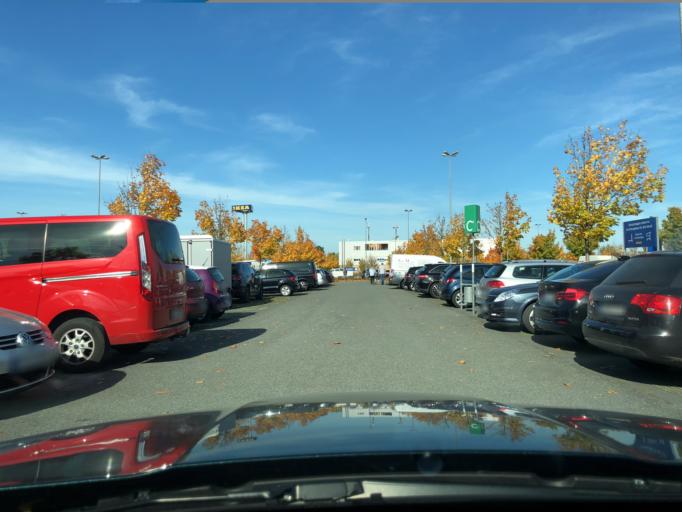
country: DE
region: Lower Saxony
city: Hasbergen
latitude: 52.2643
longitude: 7.9713
